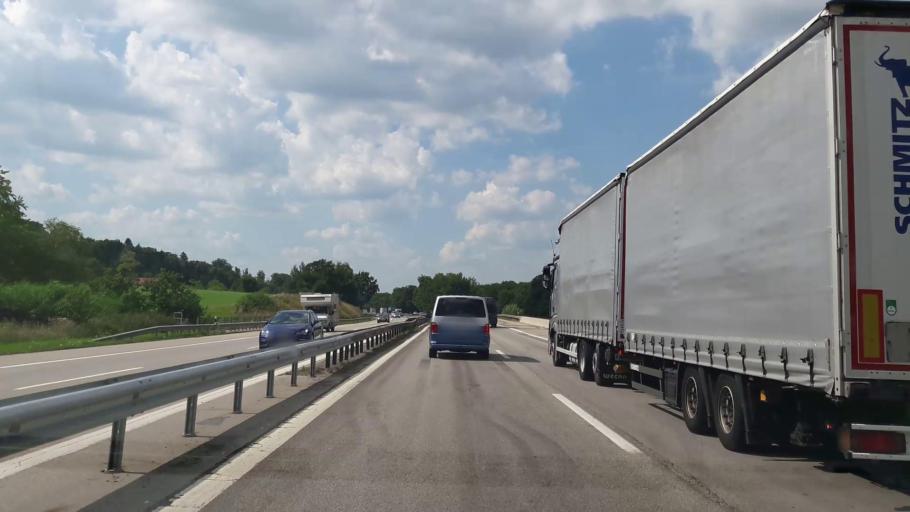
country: DE
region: Bavaria
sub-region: Upper Bavaria
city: Anger
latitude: 47.8179
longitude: 12.8298
